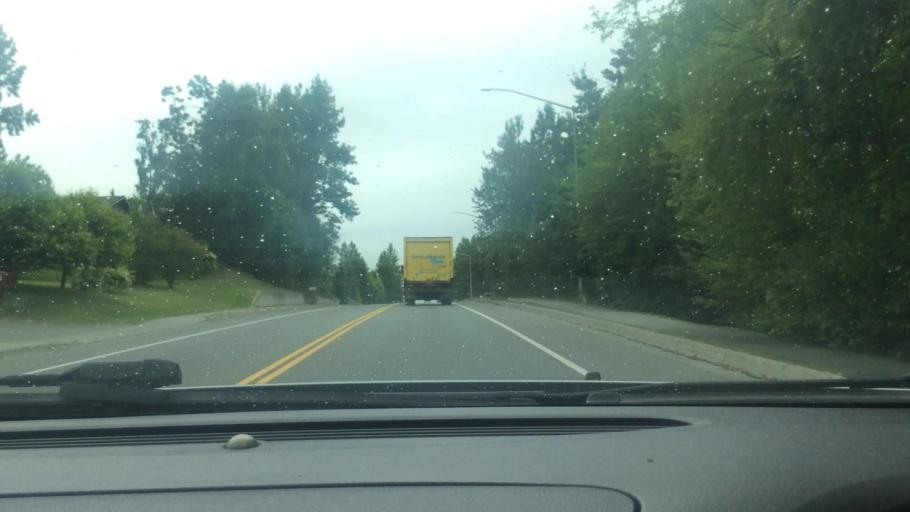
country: US
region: Alaska
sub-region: Anchorage Municipality
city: Elmendorf Air Force Base
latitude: 61.2197
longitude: -149.7561
